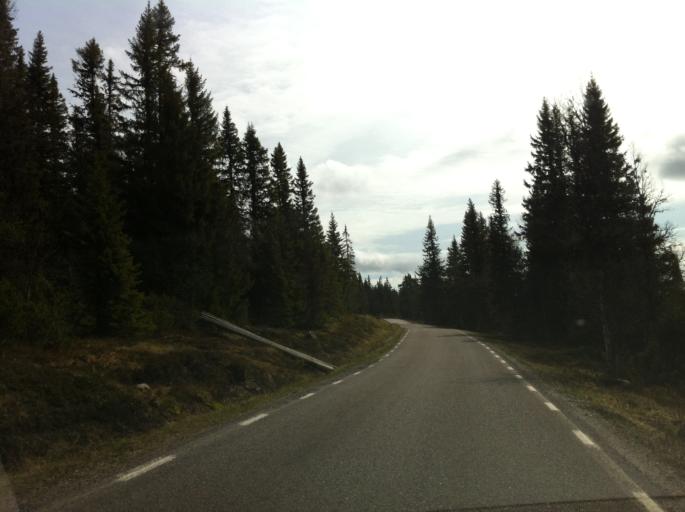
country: NO
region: Hedmark
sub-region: Engerdal
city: Engerdal
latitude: 62.3031
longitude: 12.8006
